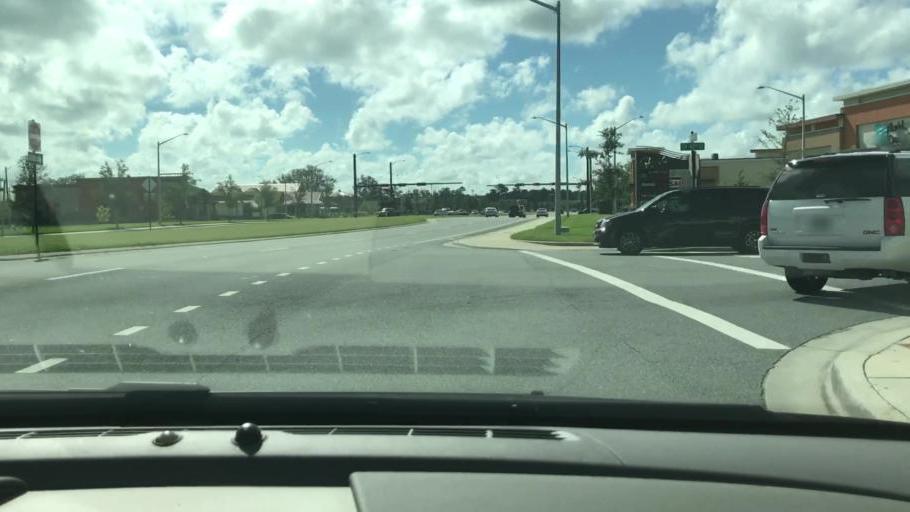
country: US
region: Florida
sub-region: Alachua County
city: Gainesville
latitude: 29.6282
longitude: -82.3864
